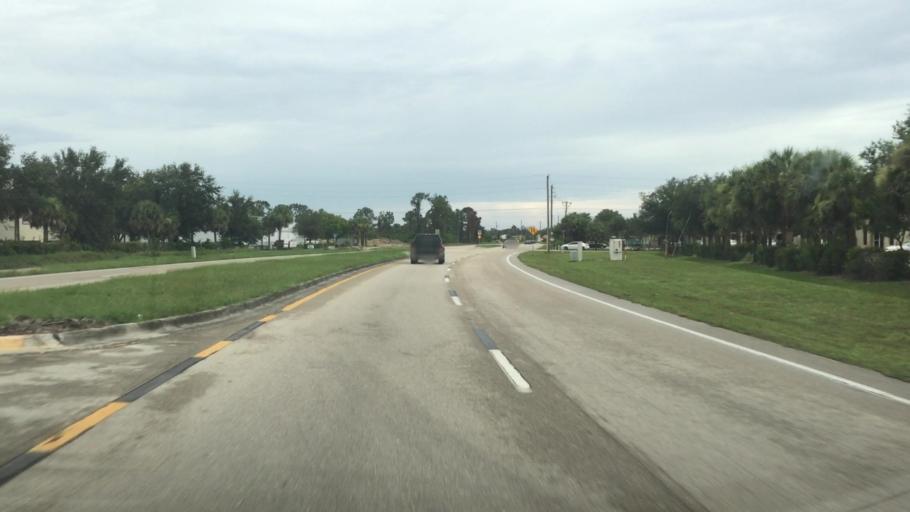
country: US
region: Florida
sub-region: Lee County
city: Gateway
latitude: 26.6184
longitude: -81.7489
